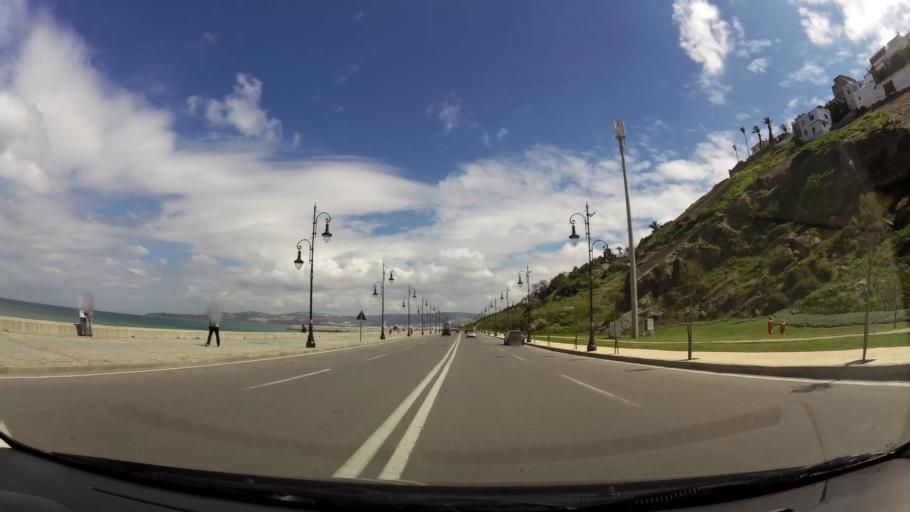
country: MA
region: Tanger-Tetouan
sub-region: Tanger-Assilah
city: Tangier
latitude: 35.7931
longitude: -5.8228
